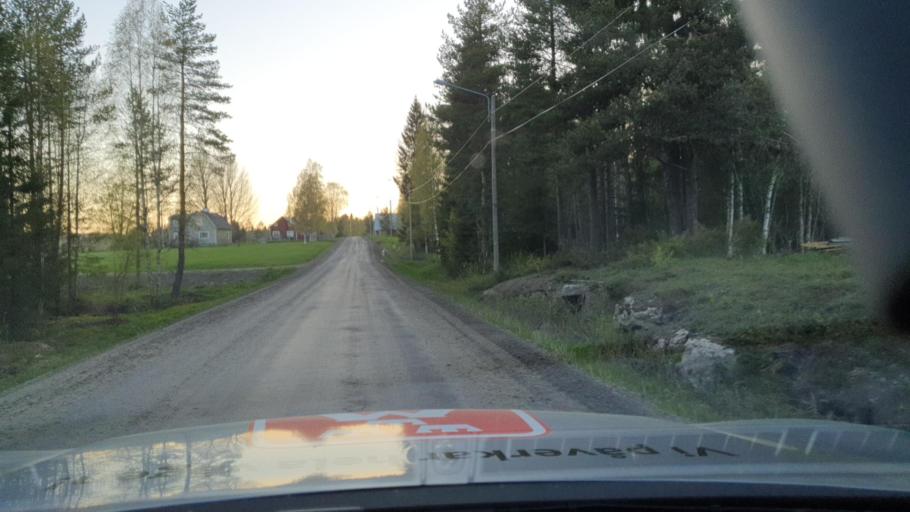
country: SE
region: Vaesternorrland
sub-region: OErnskoeldsviks Kommun
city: Ornskoldsvik
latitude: 63.5275
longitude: 18.5354
